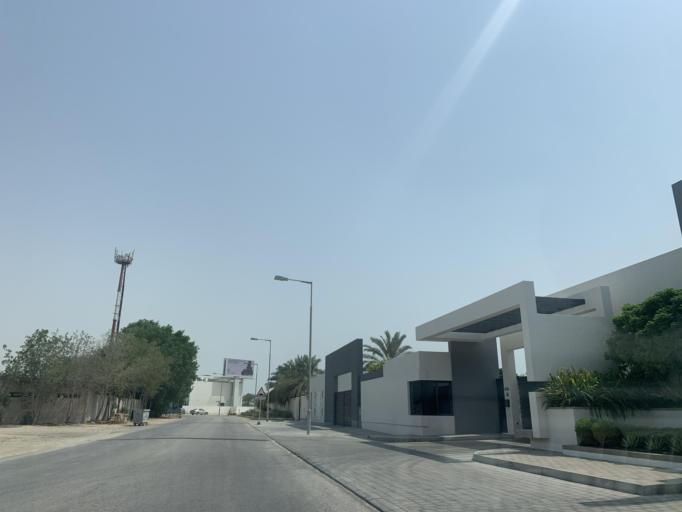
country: BH
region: Central Governorate
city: Madinat Hamad
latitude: 26.1651
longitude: 50.4723
